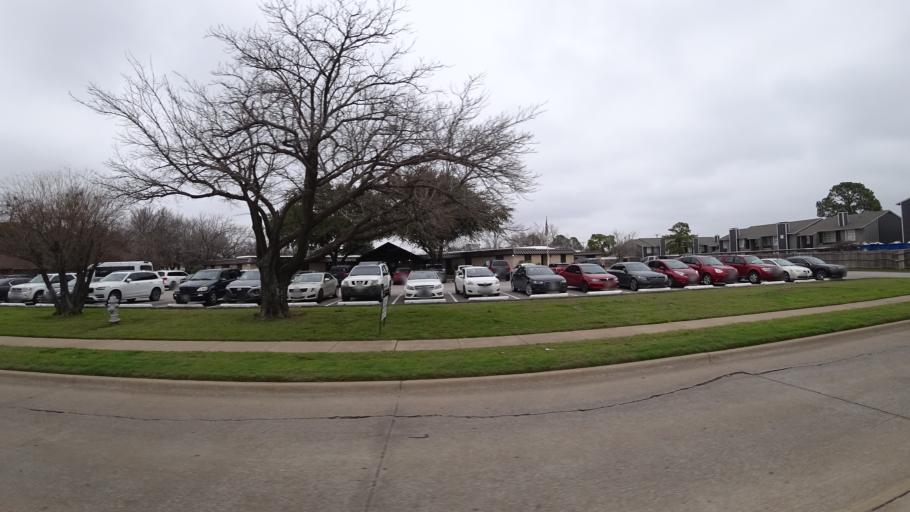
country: US
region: Texas
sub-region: Denton County
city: Lewisville
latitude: 33.0716
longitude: -97.0122
